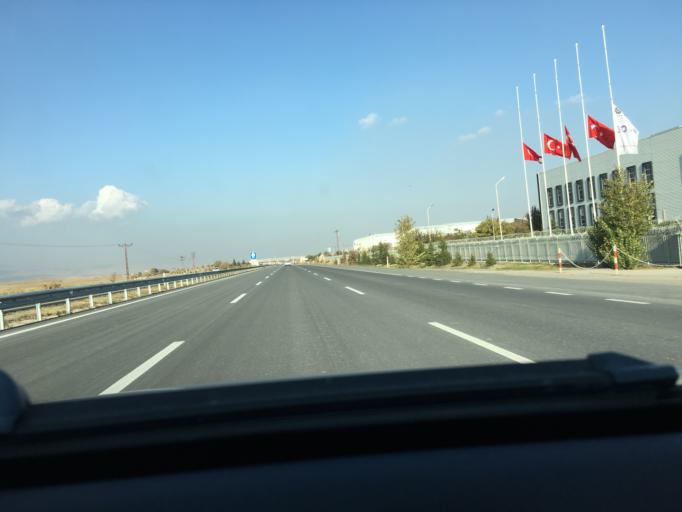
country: TR
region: Ankara
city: Polatli
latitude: 39.6464
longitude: 32.2100
